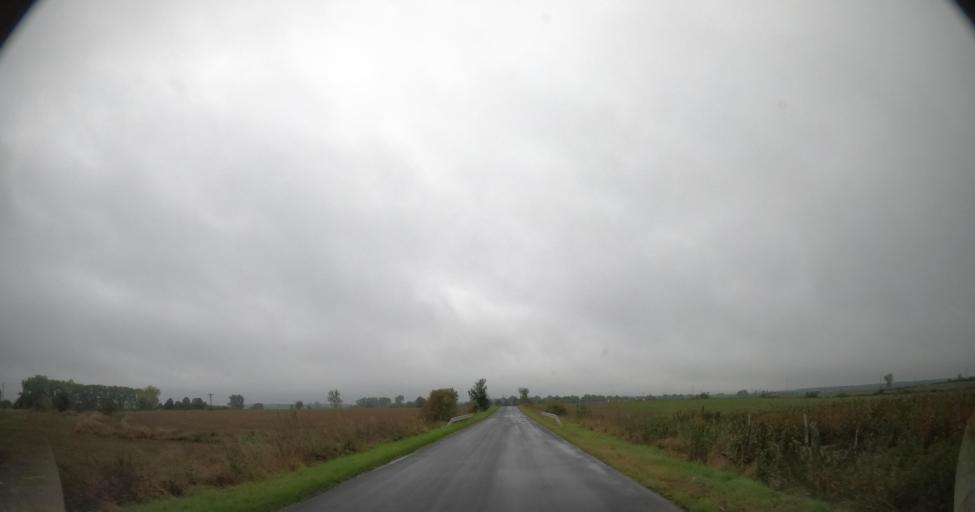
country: PL
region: West Pomeranian Voivodeship
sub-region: Powiat pyrzycki
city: Kozielice
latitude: 53.0551
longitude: 14.7779
